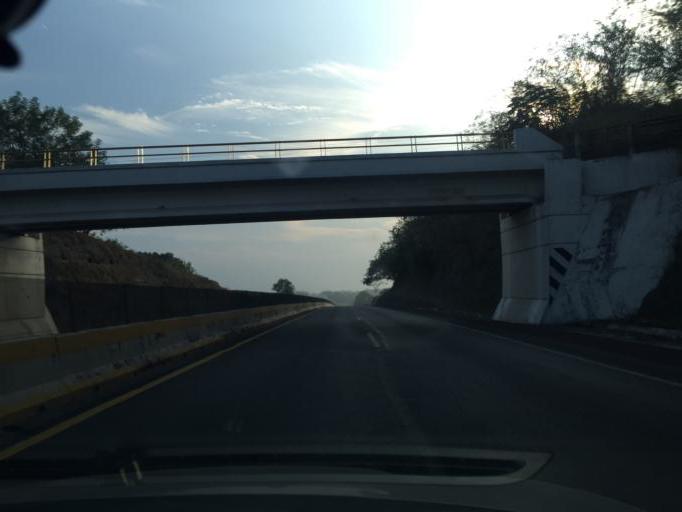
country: MX
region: Veracruz
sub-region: Tierra Blanca
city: Huixcolotla
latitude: 18.7862
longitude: -96.5464
